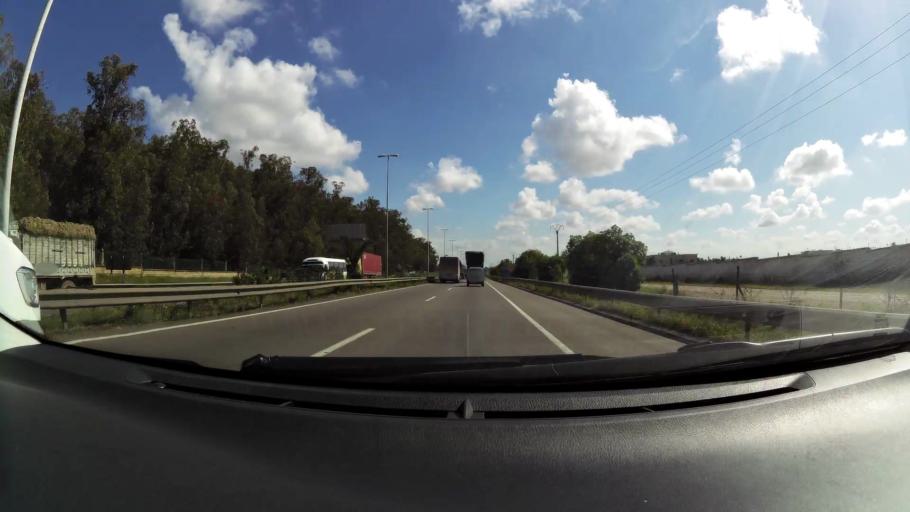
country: MA
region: Grand Casablanca
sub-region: Nouaceur
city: Bouskoura
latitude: 33.4716
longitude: -7.6334
